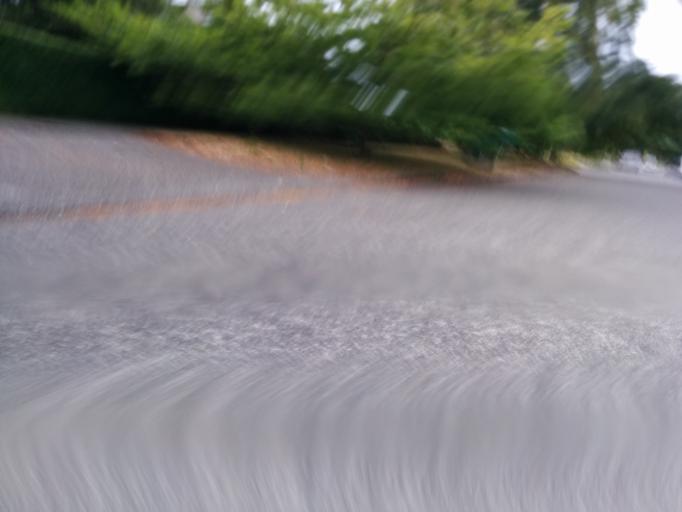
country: US
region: Washington
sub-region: King County
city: Seattle
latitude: 47.6727
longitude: -122.3714
